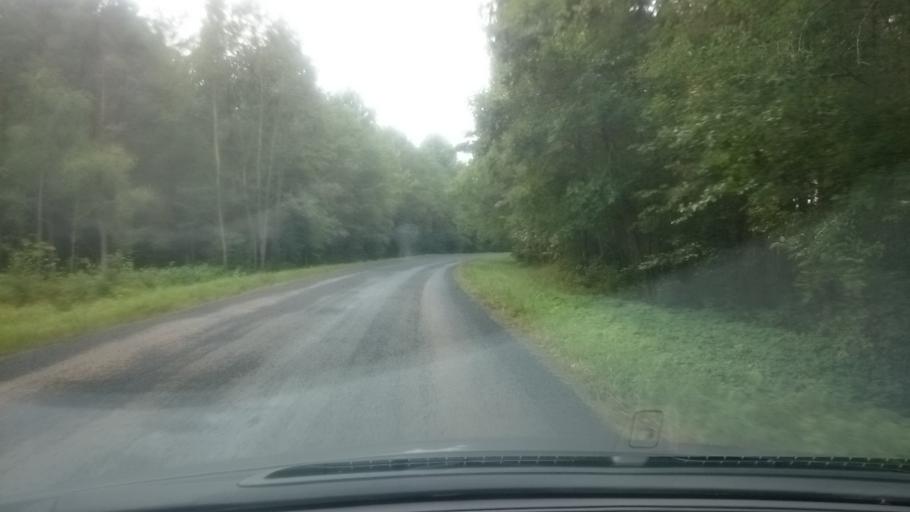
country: EE
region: Harju
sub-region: Raasiku vald
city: Raasiku
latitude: 59.4723
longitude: 25.2473
